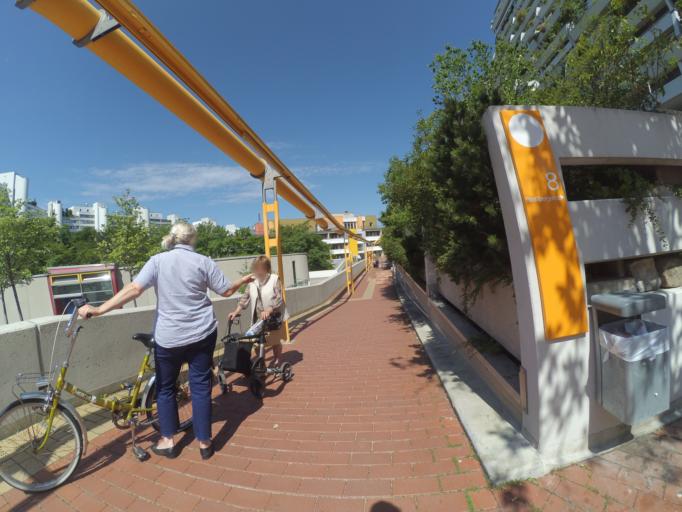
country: DE
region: Bavaria
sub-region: Upper Bavaria
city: Munich
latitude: 48.1830
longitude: 11.5516
